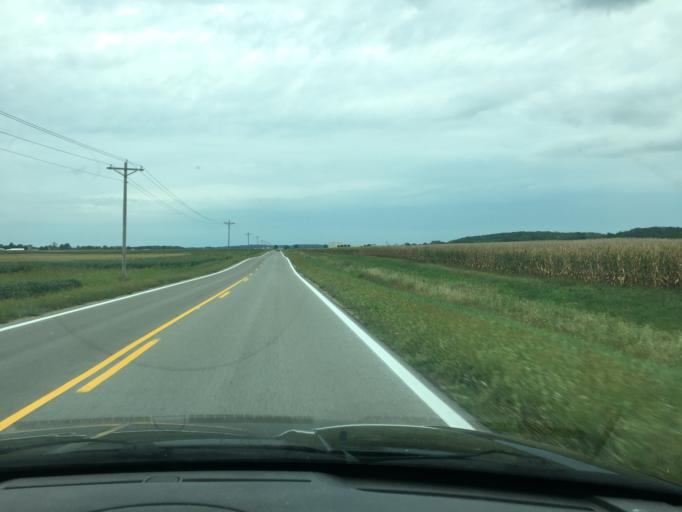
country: US
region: Ohio
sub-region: Champaign County
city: Urbana
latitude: 40.1727
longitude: -83.7831
